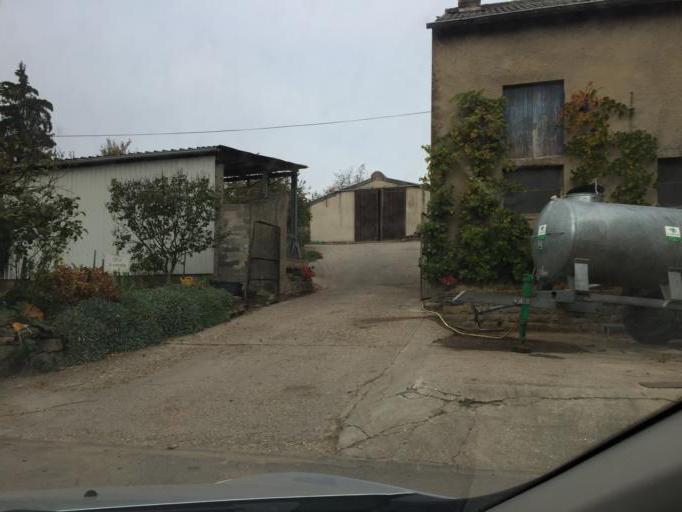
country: LU
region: Grevenmacher
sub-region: Canton de Remich
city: Bous
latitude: 49.5556
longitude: 6.3307
